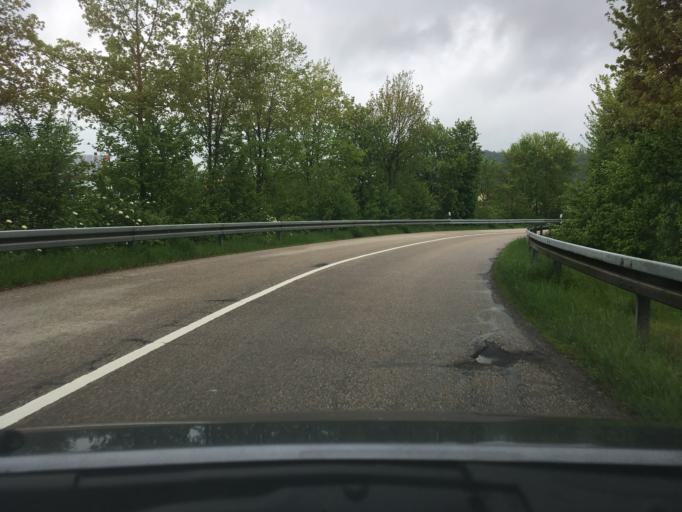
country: DE
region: Bavaria
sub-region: Upper Palatinate
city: Burglengenfeld
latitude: 49.2073
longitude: 12.0184
